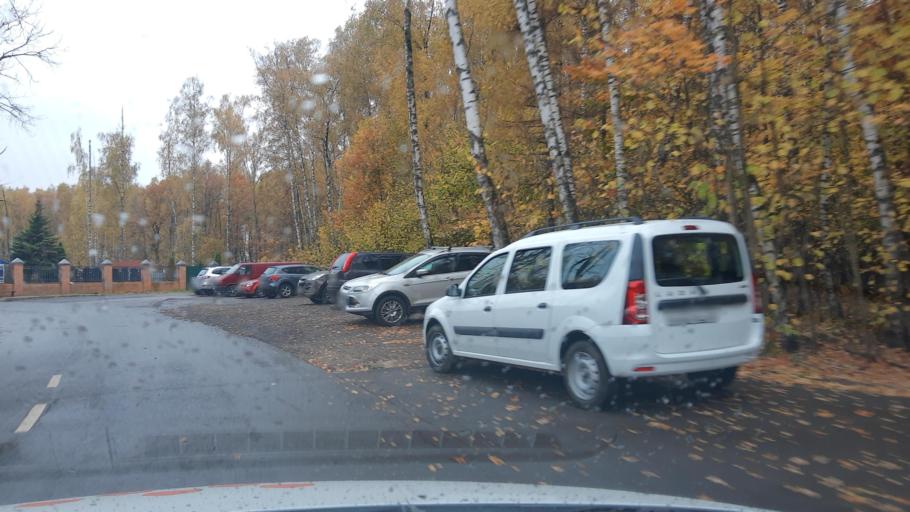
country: RU
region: Moskovskaya
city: Shcherbinka
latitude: 55.5296
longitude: 37.5628
